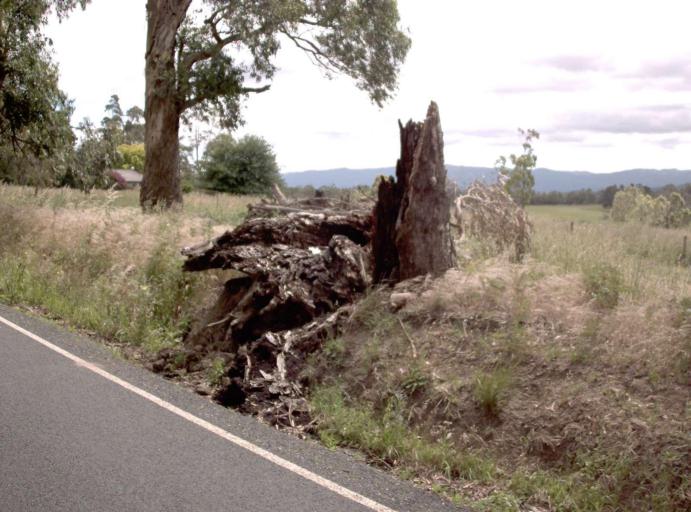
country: AU
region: Victoria
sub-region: Latrobe
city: Moe
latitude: -38.0348
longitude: 146.1657
